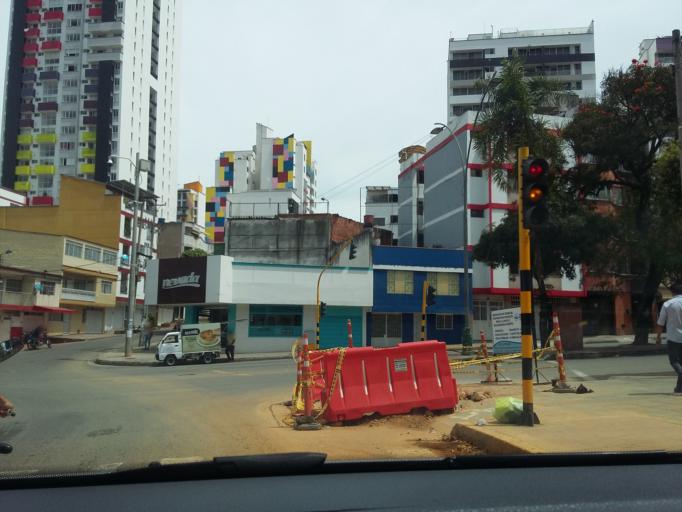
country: CO
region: Santander
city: Bucaramanga
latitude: 7.1296
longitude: -73.1142
